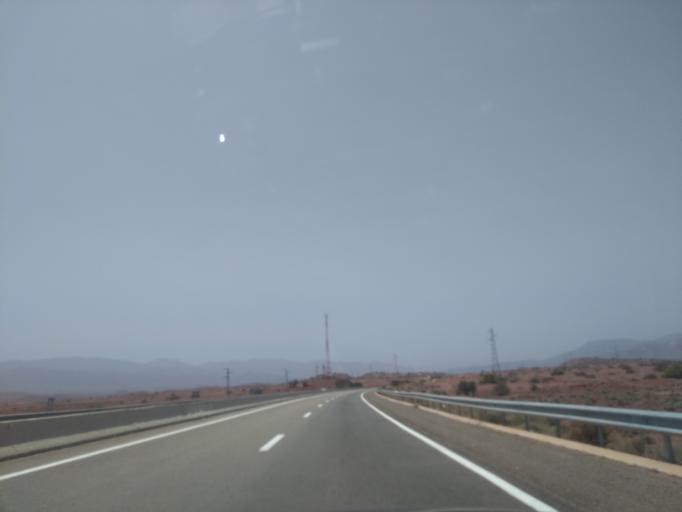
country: MA
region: Marrakech-Tensift-Al Haouz
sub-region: Chichaoua
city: Timezgadiouine
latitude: 30.8807
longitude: -9.0796
